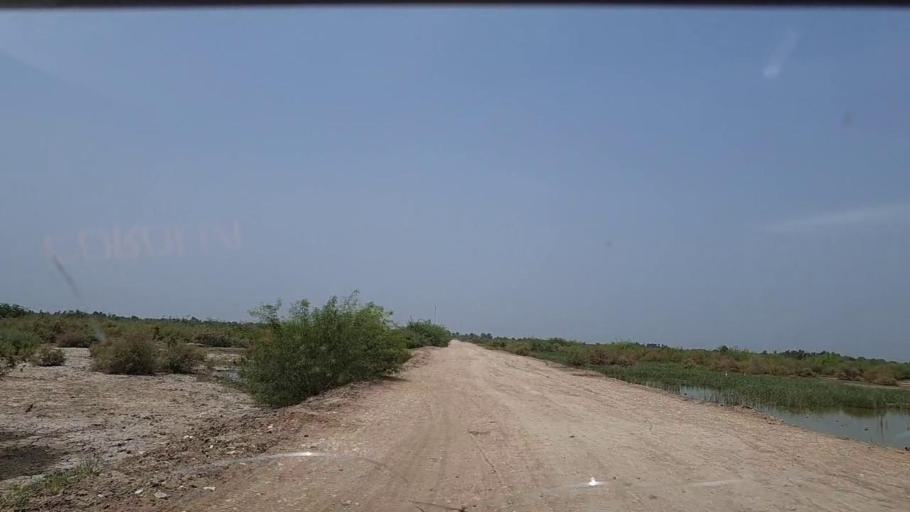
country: PK
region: Sindh
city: Adilpur
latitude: 27.9091
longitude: 69.2181
